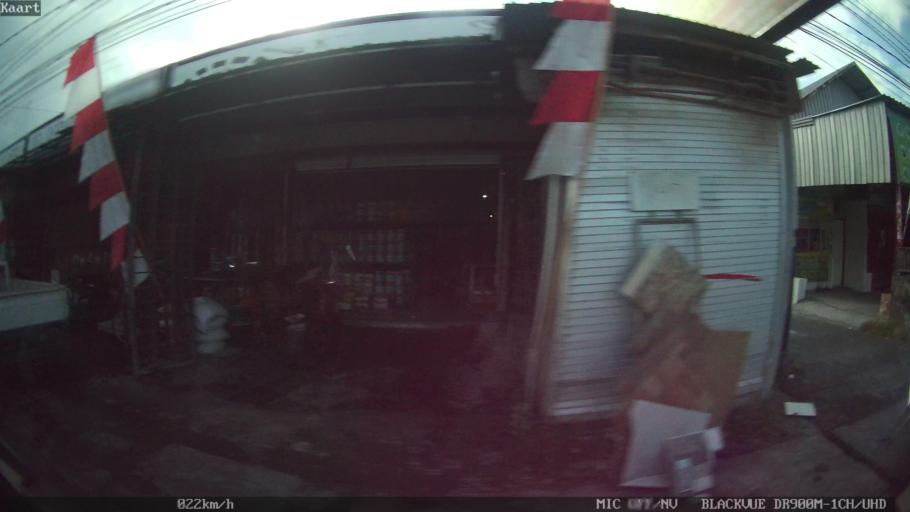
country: ID
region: Bali
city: Karyadharma
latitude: -8.6979
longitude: 115.1921
